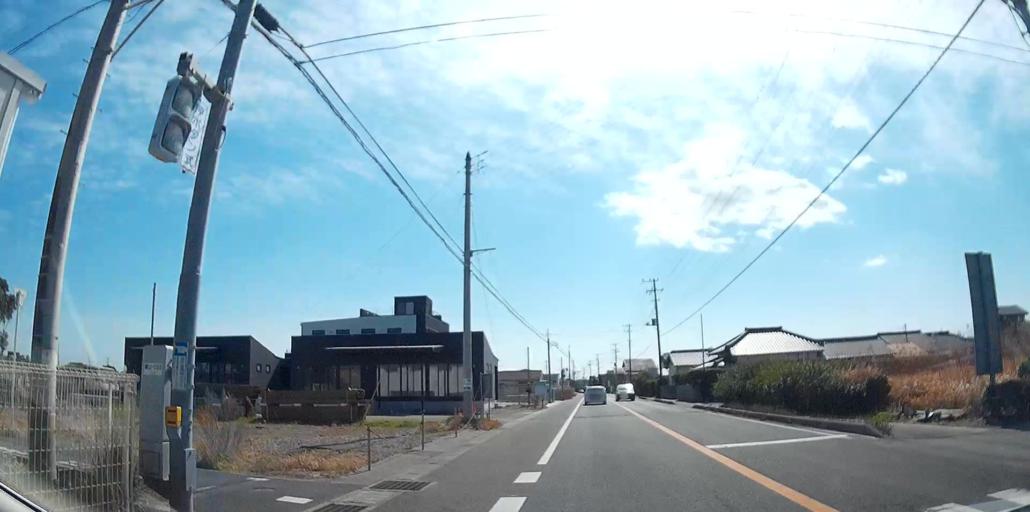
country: JP
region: Chiba
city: Tateyama
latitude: 35.0159
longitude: 139.8587
